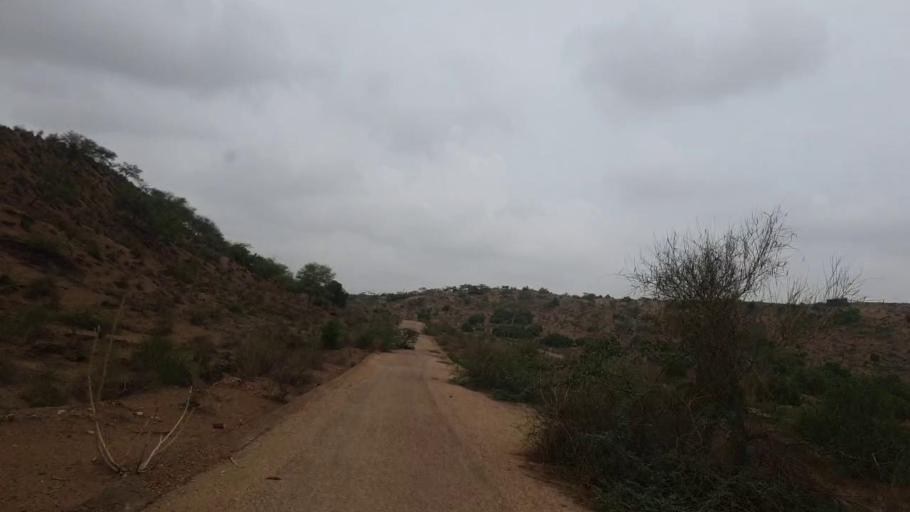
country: PK
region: Sindh
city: Diplo
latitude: 24.5131
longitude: 69.4902
